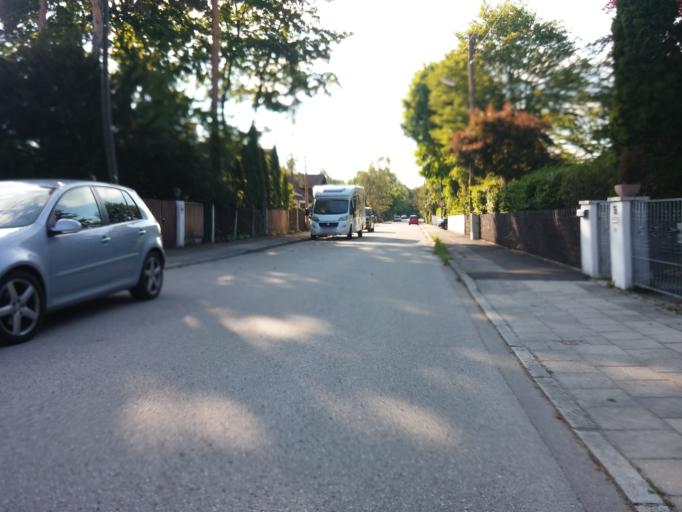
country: DE
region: Bavaria
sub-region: Upper Bavaria
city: Vaterstetten
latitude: 48.0996
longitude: 11.7569
